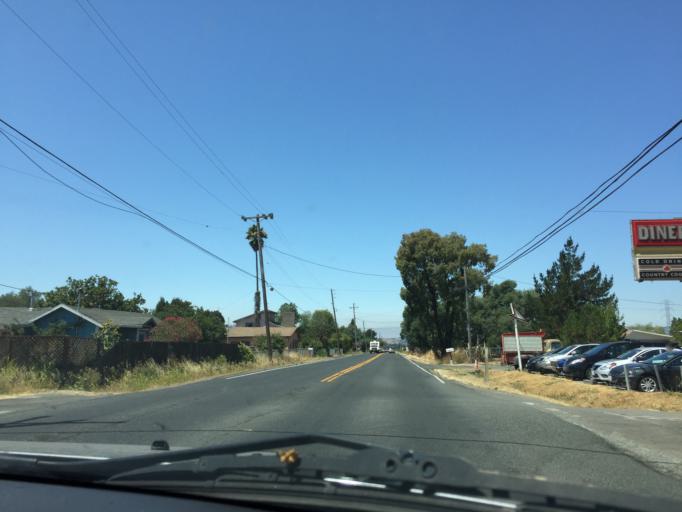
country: US
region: California
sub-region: Sonoma County
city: Sonoma
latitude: 38.2466
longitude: -122.4166
